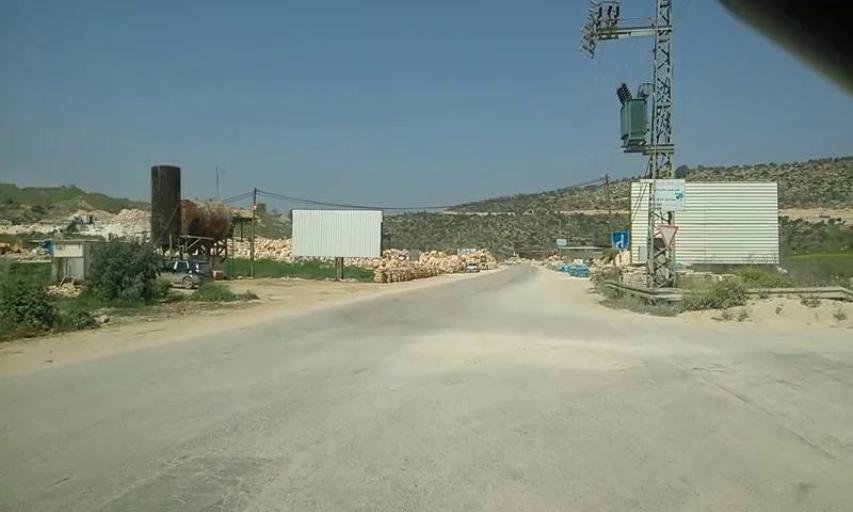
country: PS
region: West Bank
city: Az Zababidah
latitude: 32.4005
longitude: 35.3182
